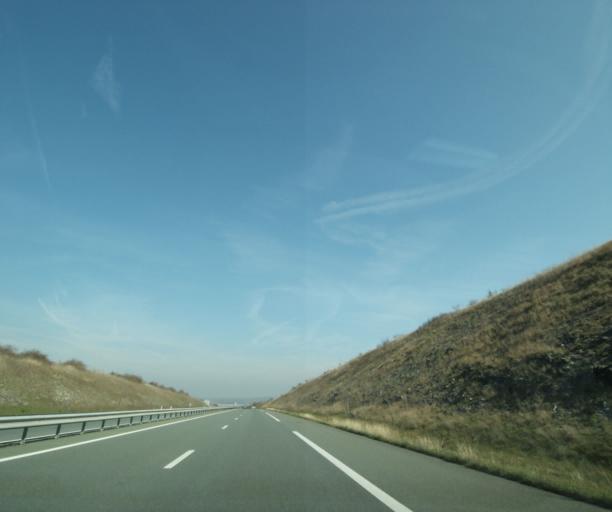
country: FR
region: Midi-Pyrenees
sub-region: Departement du Lot
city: Le Vigan
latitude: 44.6698
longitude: 1.5706
